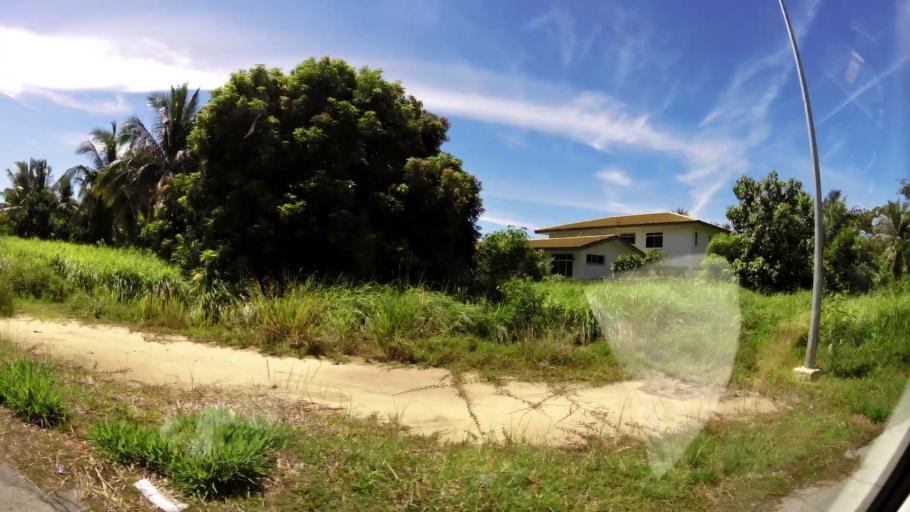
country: BN
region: Brunei and Muara
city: Bandar Seri Begawan
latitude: 5.0345
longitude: 115.0696
